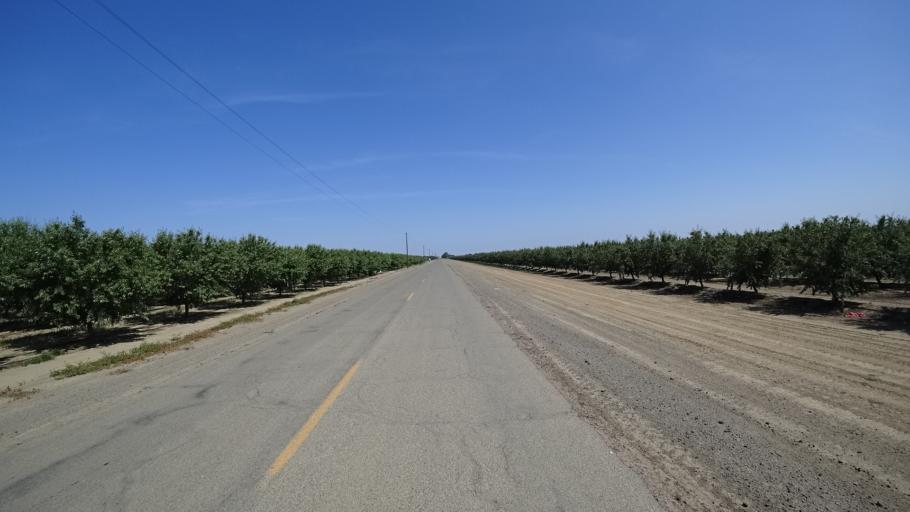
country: US
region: California
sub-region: Kings County
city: Kettleman City
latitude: 36.0807
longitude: -120.0037
